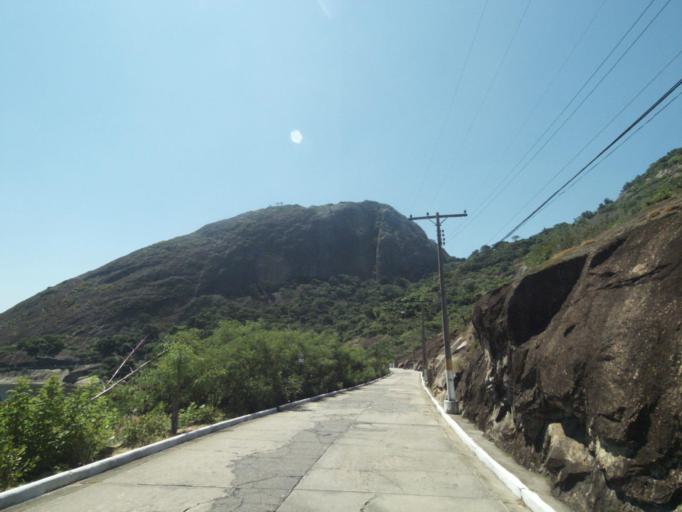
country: BR
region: Rio de Janeiro
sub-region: Niteroi
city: Niteroi
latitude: -22.9361
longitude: -43.1276
